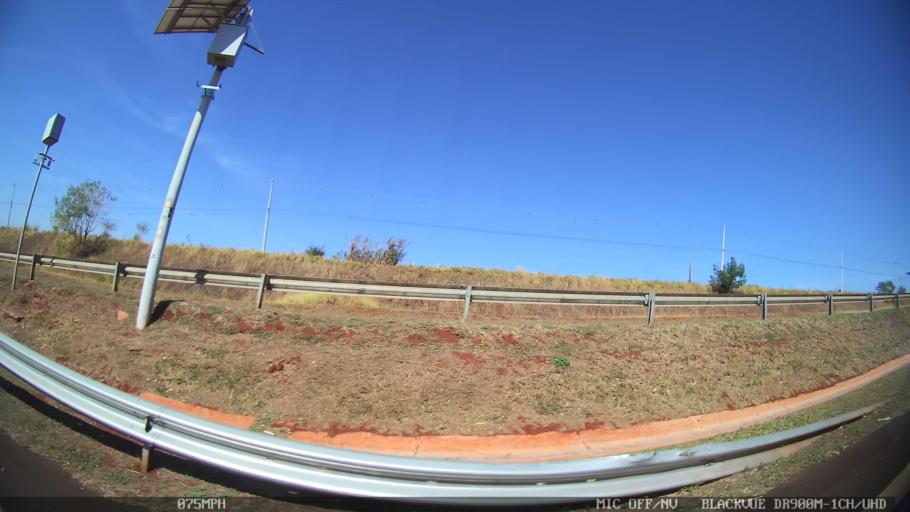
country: BR
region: Sao Paulo
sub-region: Ribeirao Preto
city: Ribeirao Preto
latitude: -21.1434
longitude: -47.8728
